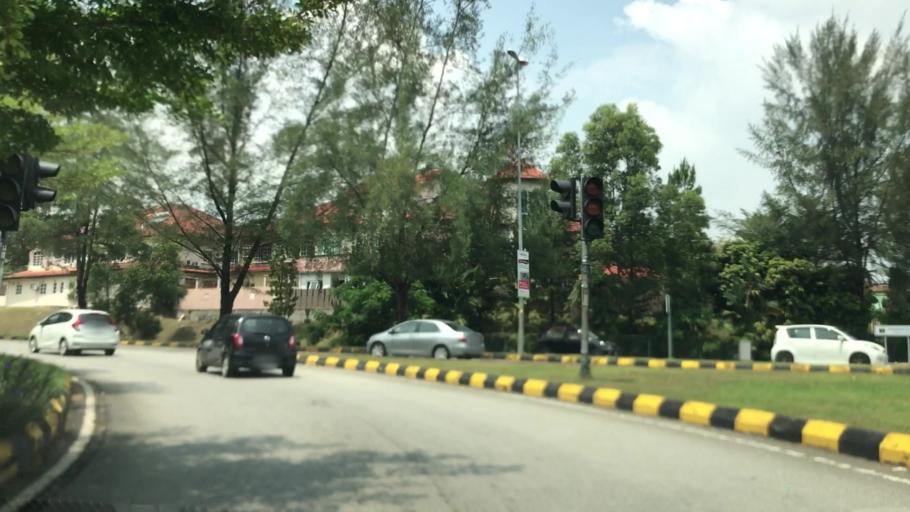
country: MY
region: Selangor
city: Subang Jaya
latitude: 3.0180
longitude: 101.6248
